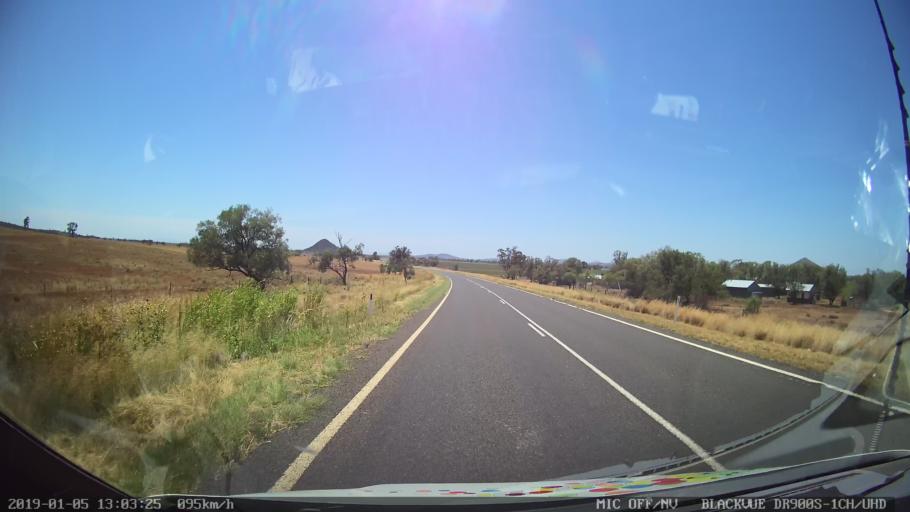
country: AU
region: New South Wales
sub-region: Gunnedah
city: Gunnedah
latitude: -31.1111
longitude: 149.8271
